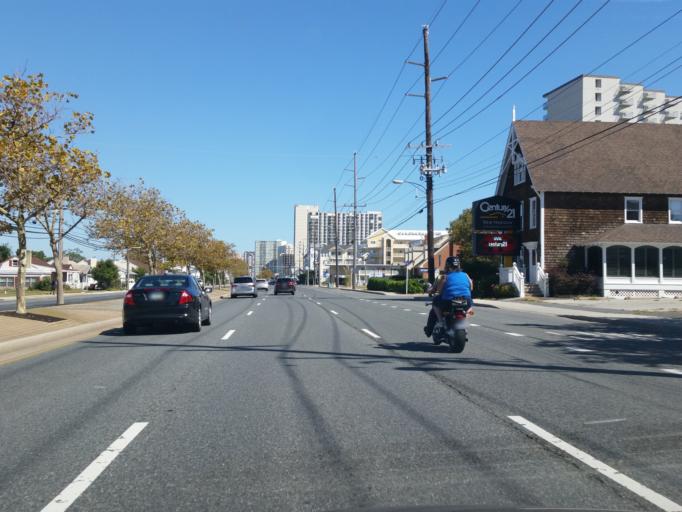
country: US
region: Maryland
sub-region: Worcester County
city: Ocean City
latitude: 38.4042
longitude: -75.0601
